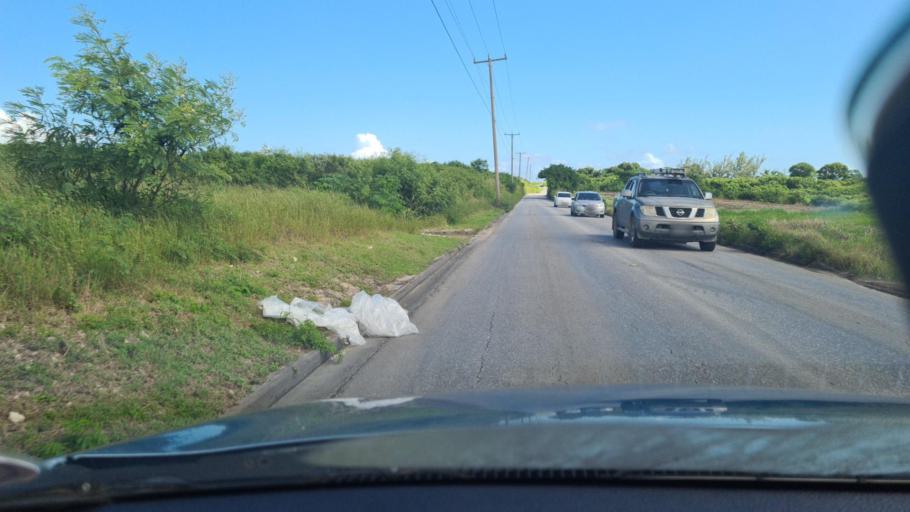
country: BB
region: Saint Philip
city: Crane
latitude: 13.1168
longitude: -59.4641
